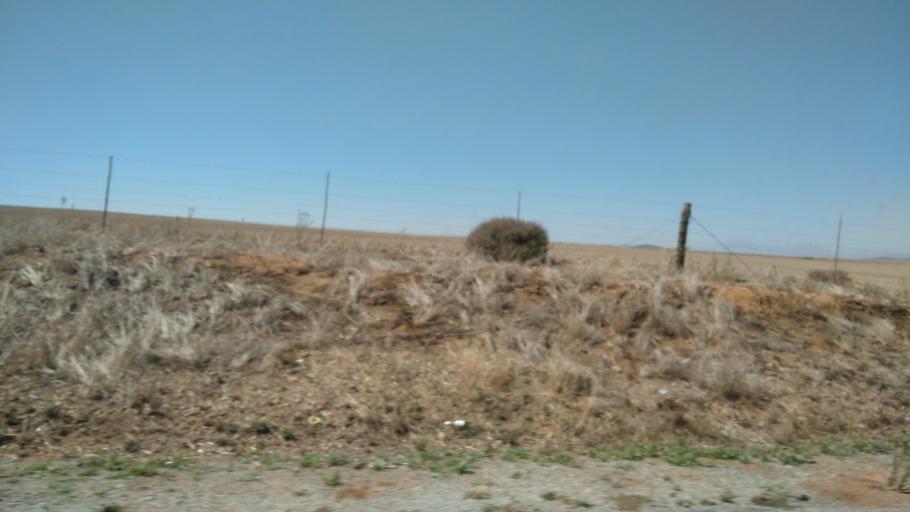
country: ZA
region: Western Cape
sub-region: West Coast District Municipality
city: Moorreesburg
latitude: -33.2234
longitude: 18.5481
